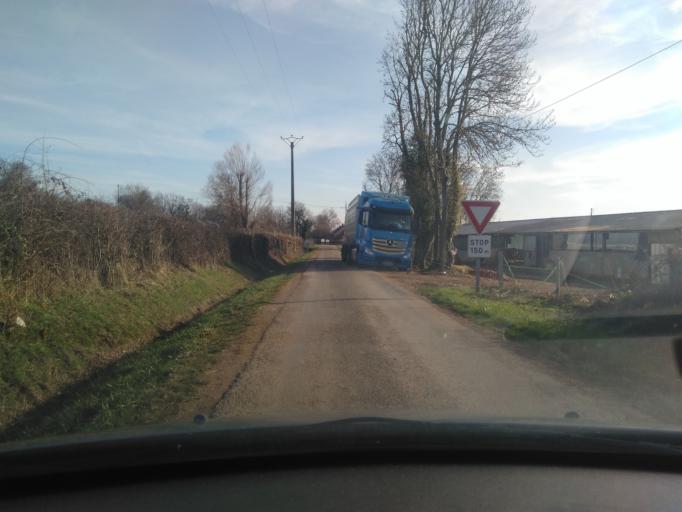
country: FR
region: Bourgogne
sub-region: Departement de la Nievre
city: Saint-Parize-le-Chatel
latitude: 46.8311
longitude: 3.2450
